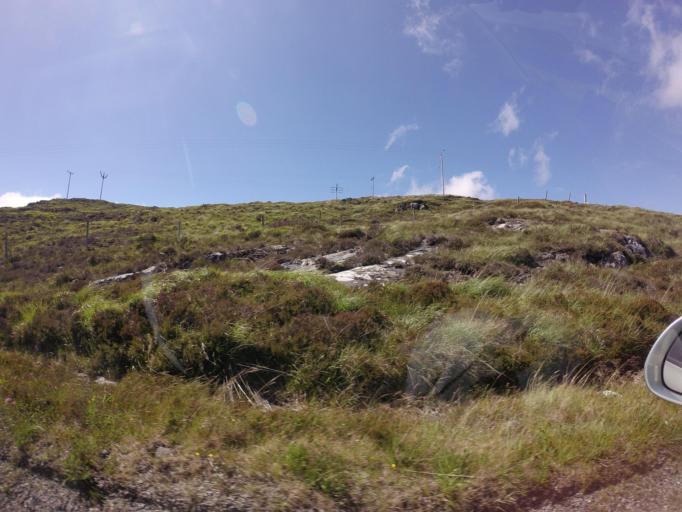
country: GB
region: Scotland
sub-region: Eilean Siar
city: Stornoway
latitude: 58.1359
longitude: -6.5088
